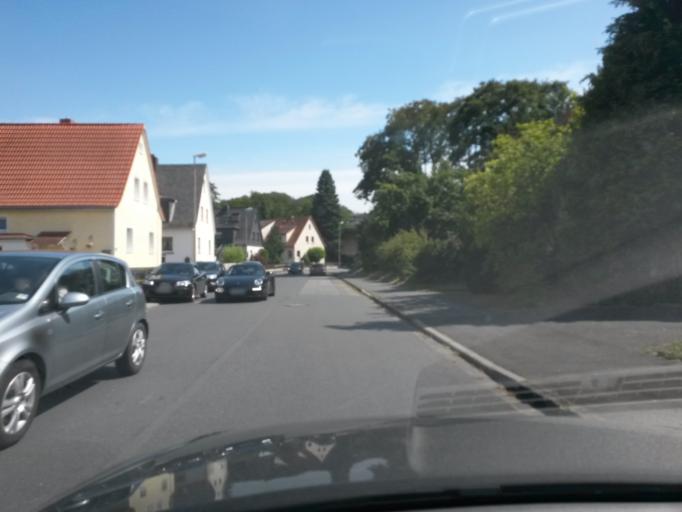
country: DE
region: Hesse
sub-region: Regierungsbezirk Darmstadt
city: Neu-Anspach
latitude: 50.2992
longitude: 8.5158
